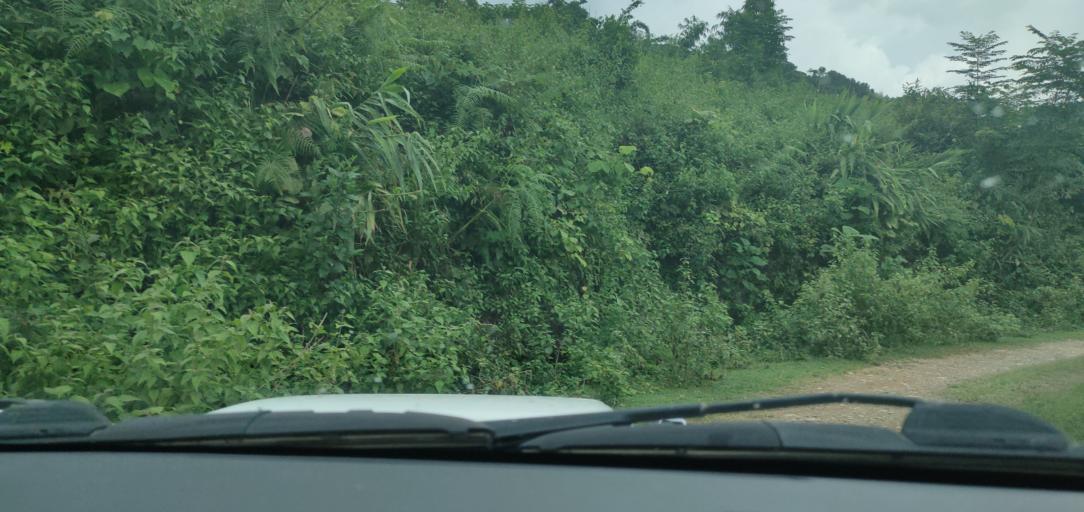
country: LA
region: Phongsali
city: Phongsali
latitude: 21.4391
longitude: 102.3293
